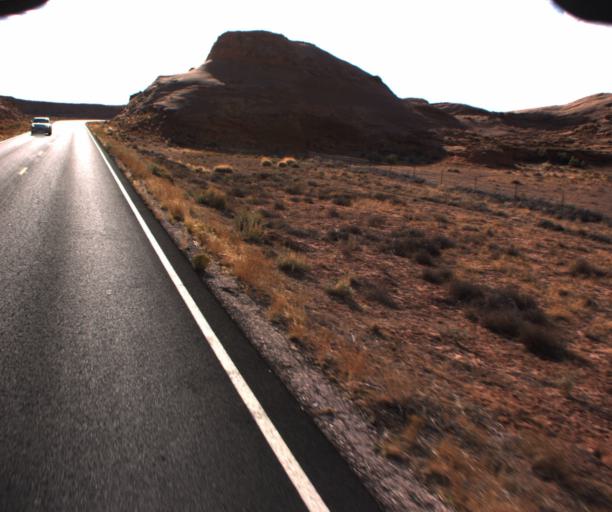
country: US
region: Arizona
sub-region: Apache County
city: Many Farms
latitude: 36.7678
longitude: -109.6563
